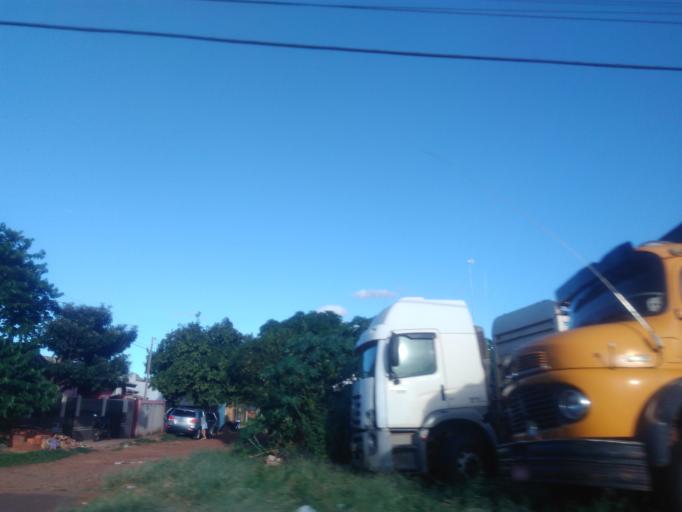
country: BR
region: Mato Grosso do Sul
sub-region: Ponta Pora
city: Ponta Pora
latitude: -22.5112
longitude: -55.7289
